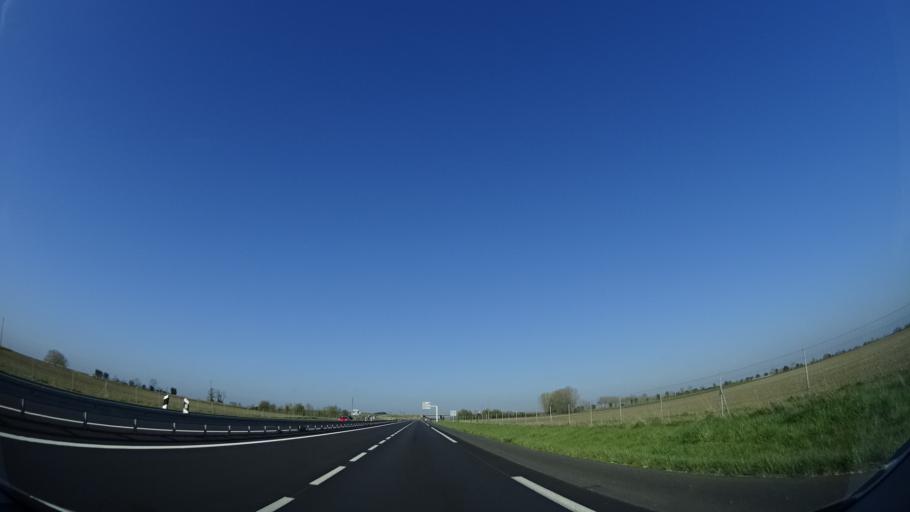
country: FR
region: Pays de la Loire
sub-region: Departement de Maine-et-Loire
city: Saint-Jean
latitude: 47.2844
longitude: -0.3657
